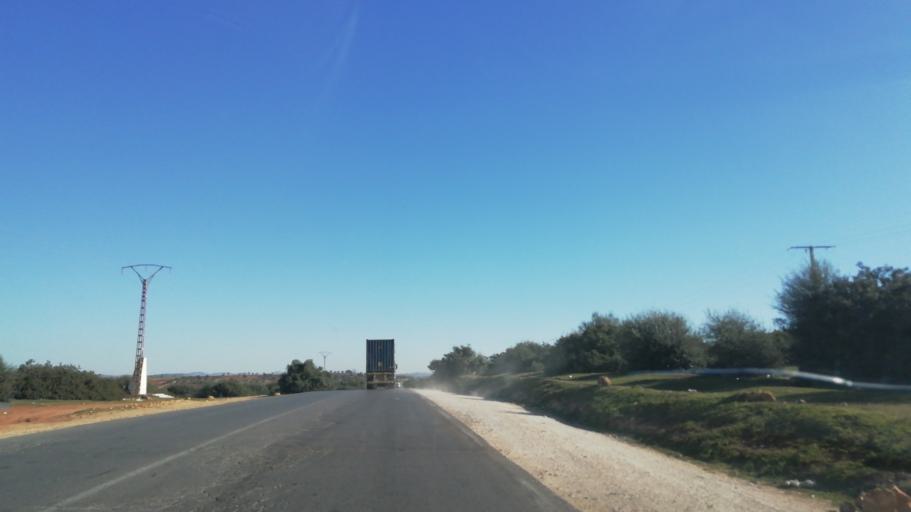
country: DZ
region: Relizane
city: Smala
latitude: 35.6912
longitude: 0.7905
